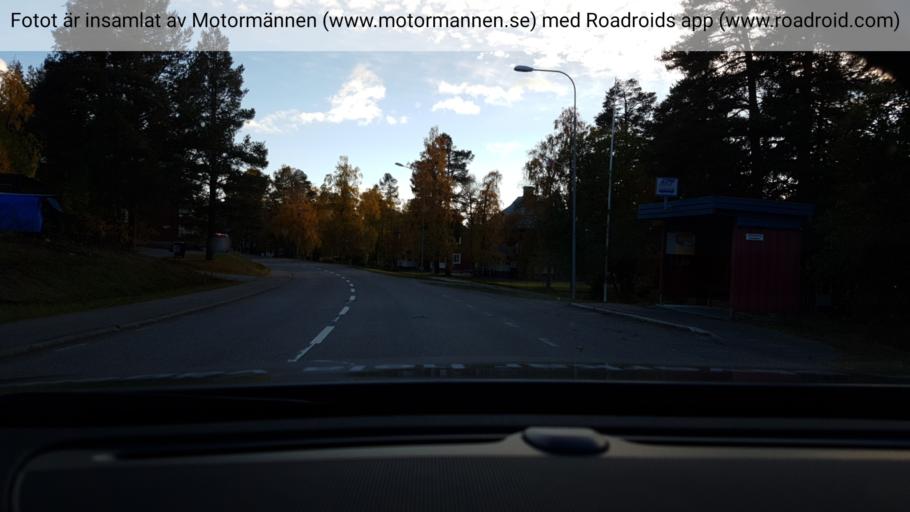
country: SE
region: Norrbotten
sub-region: Jokkmokks Kommun
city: Jokkmokk
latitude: 66.9526
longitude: 19.7975
